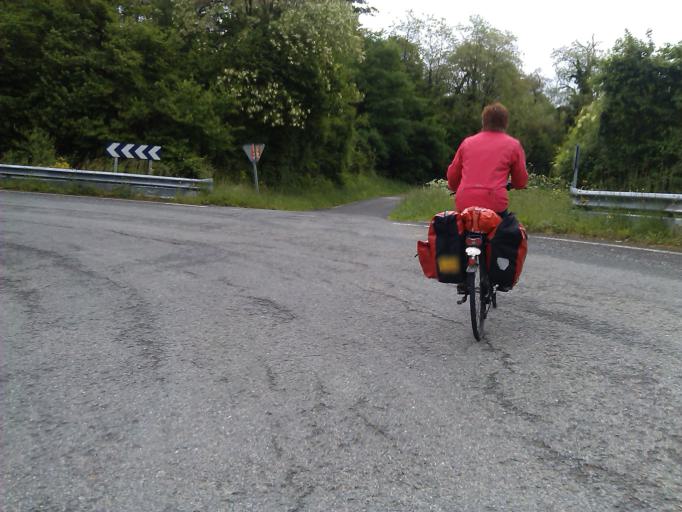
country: ES
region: Navarre
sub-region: Provincia de Navarra
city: Lekunberri
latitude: 42.9980
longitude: -1.8884
